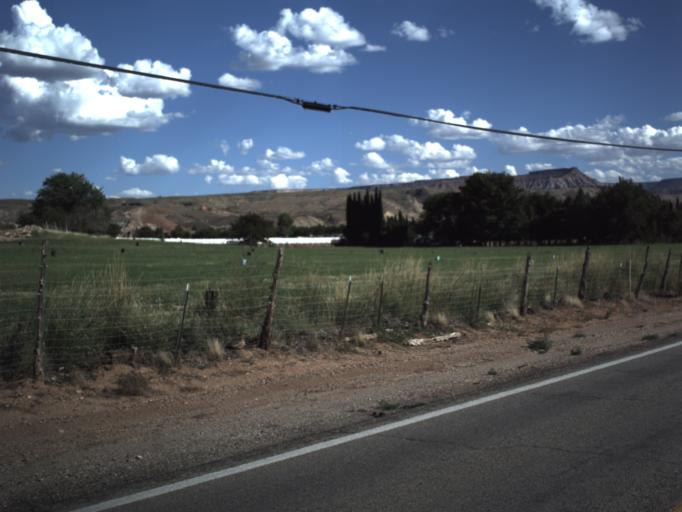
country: US
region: Utah
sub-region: Washington County
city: Toquerville
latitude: 37.2379
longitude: -113.2810
